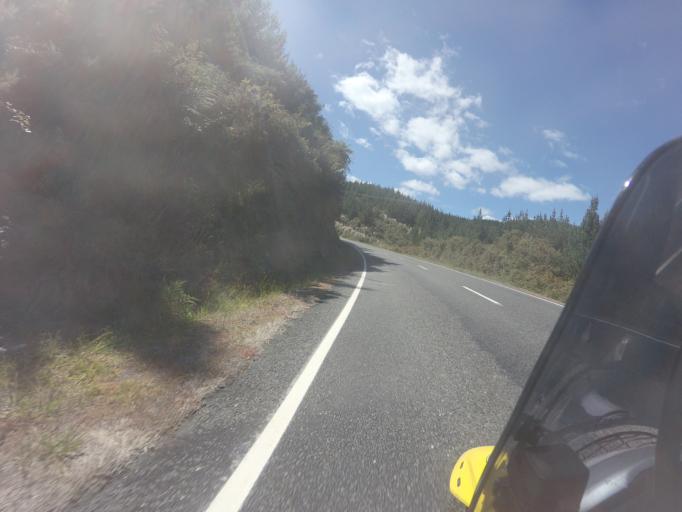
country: NZ
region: Bay of Plenty
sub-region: Whakatane District
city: Murupara
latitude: -38.2845
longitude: 176.8149
